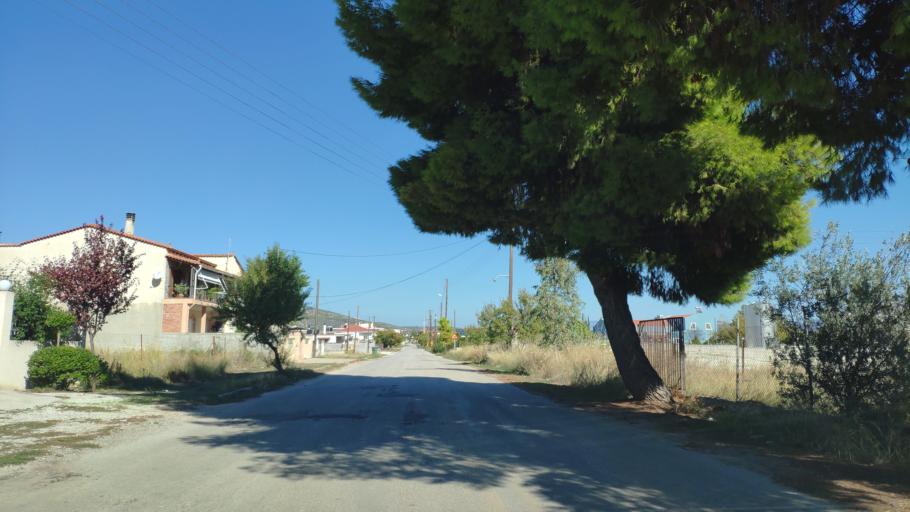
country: GR
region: Peloponnese
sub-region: Nomos Korinthias
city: Khiliomodhi
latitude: 37.8018
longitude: 22.8691
